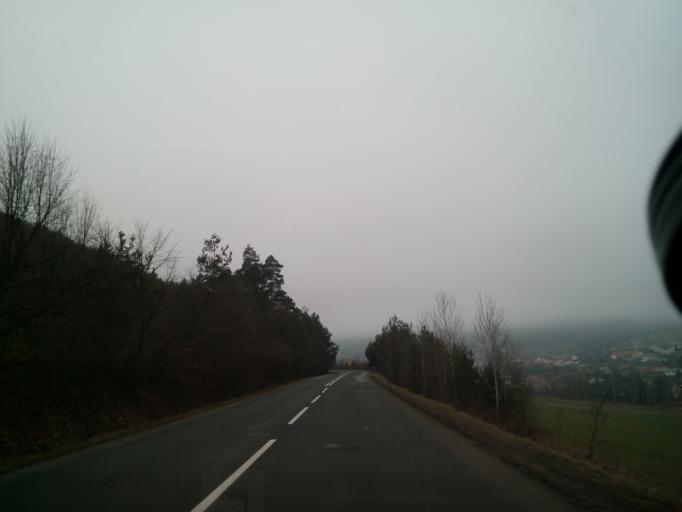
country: SK
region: Kosicky
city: Krompachy
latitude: 48.9205
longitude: 20.9264
